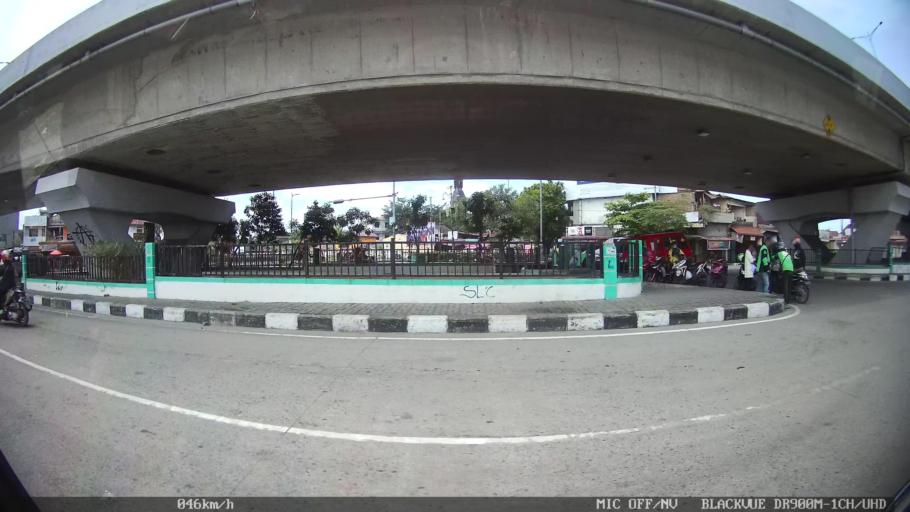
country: ID
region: North Sumatra
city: Medan
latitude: 3.5404
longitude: 98.6526
